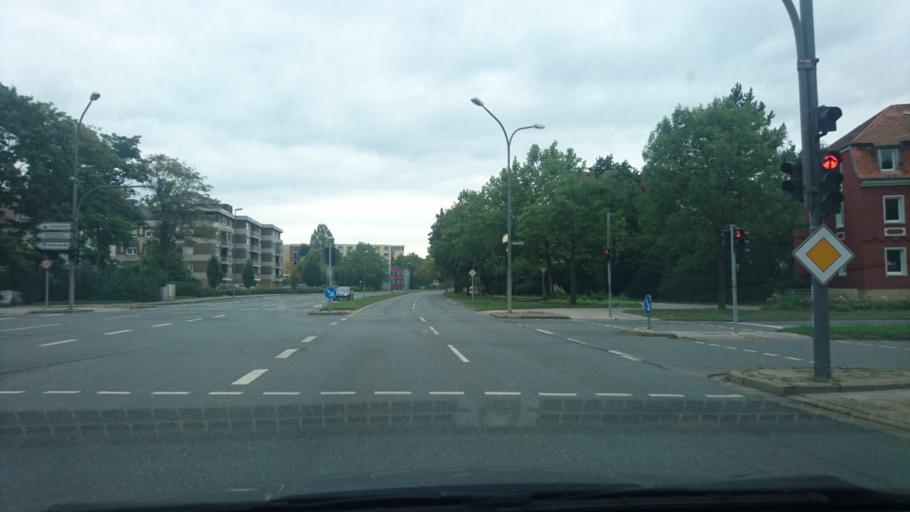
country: DE
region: Bavaria
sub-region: Upper Franconia
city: Bayreuth
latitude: 49.9355
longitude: 11.5804
